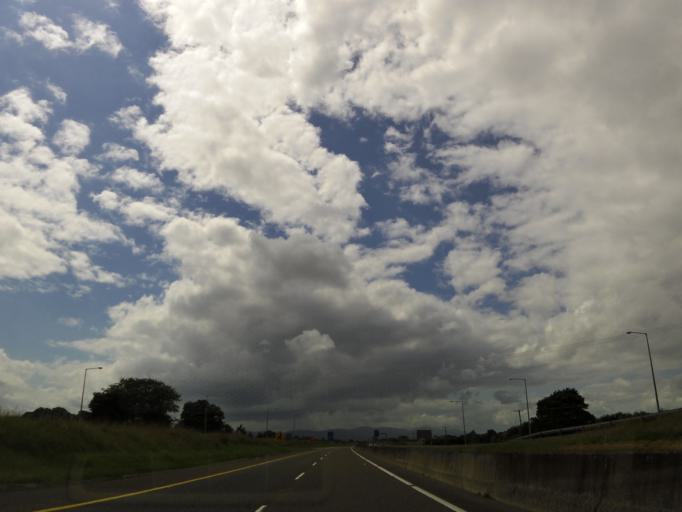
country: IE
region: Munster
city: Cashel
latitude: 52.5076
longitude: -7.8728
